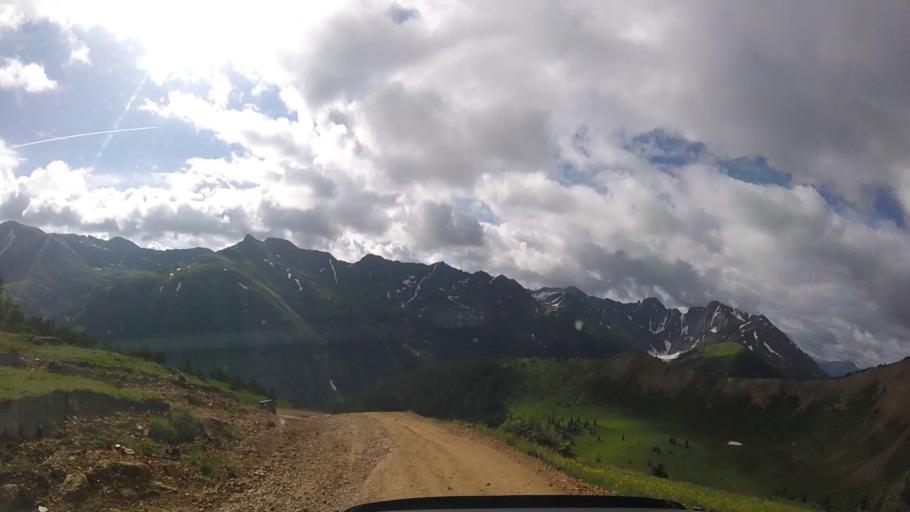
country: US
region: Colorado
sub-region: San Juan County
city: Silverton
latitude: 37.9063
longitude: -107.6584
